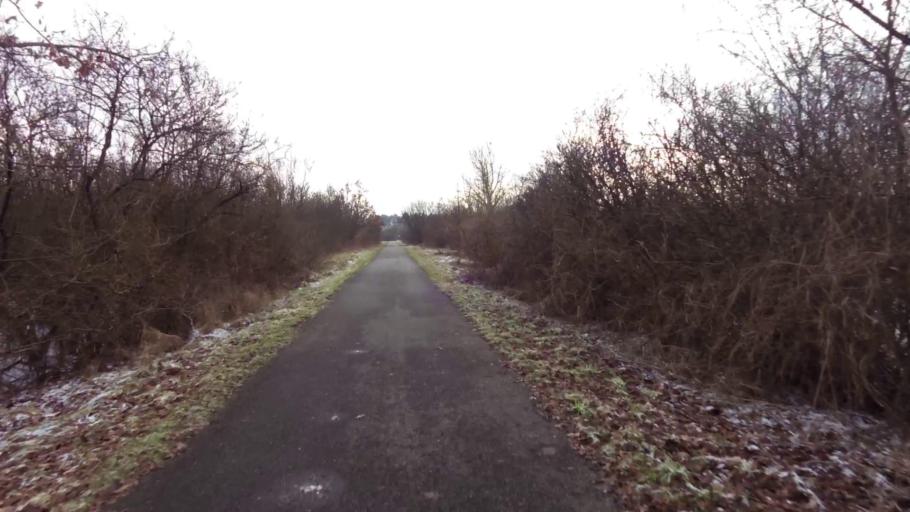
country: PL
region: West Pomeranian Voivodeship
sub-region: Powiat drawski
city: Zlocieniec
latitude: 53.5896
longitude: 16.0477
